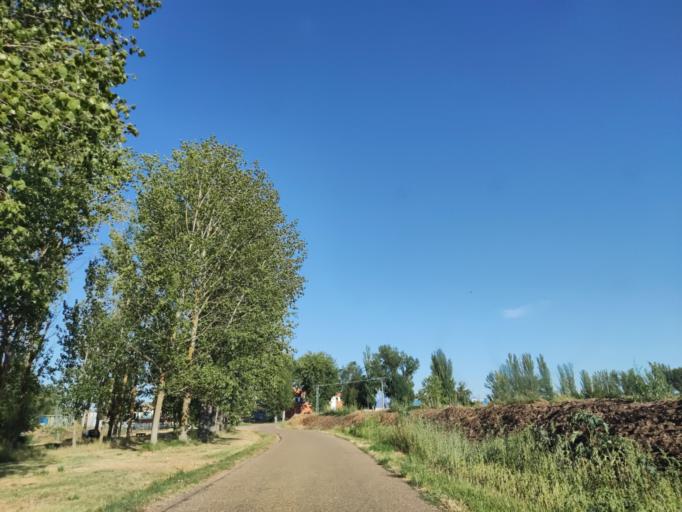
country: ES
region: Castille and Leon
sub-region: Provincia de Zamora
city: Villaralbo
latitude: 41.5019
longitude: -5.6885
